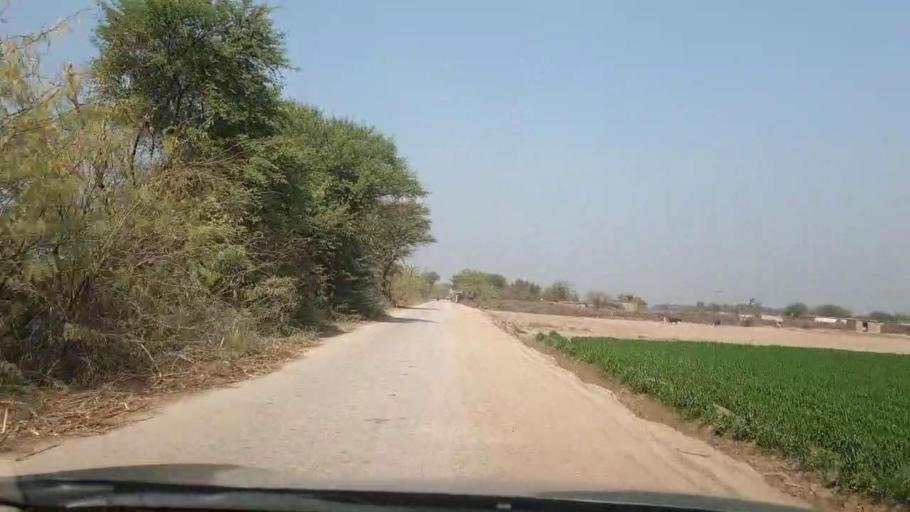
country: PK
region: Sindh
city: Tando Allahyar
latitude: 25.4985
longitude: 68.7960
